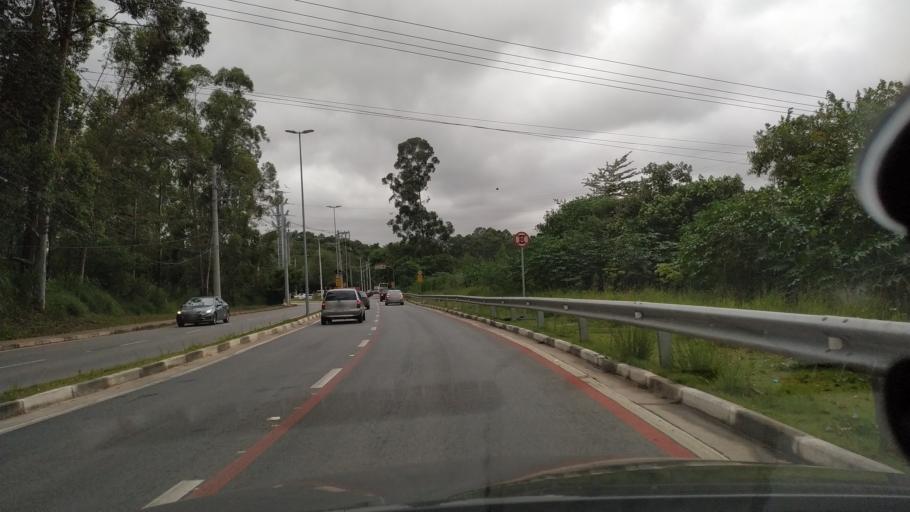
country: BR
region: Sao Paulo
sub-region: Barueri
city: Barueri
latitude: -23.4878
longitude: -46.8708
